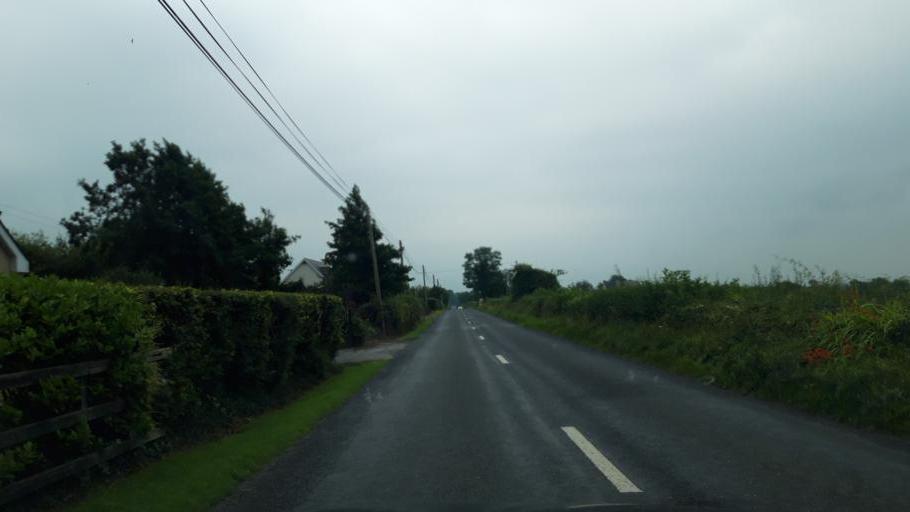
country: IE
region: Munster
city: Fethard
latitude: 52.5225
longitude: -7.6827
